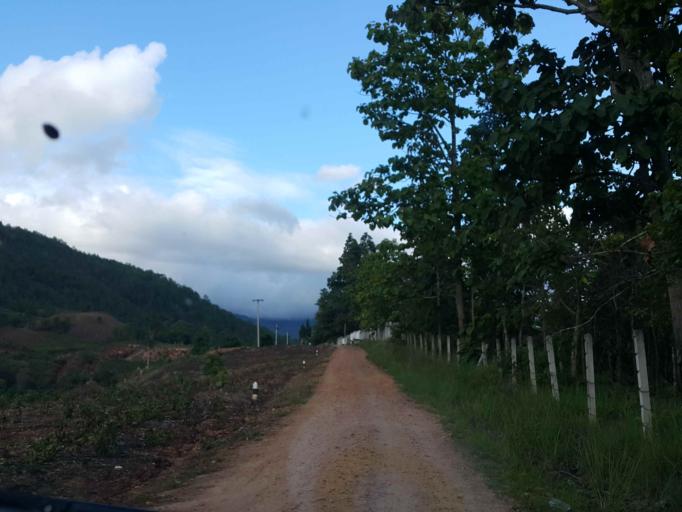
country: TH
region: Chiang Mai
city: Mae Chaem
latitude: 18.5260
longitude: 98.3933
